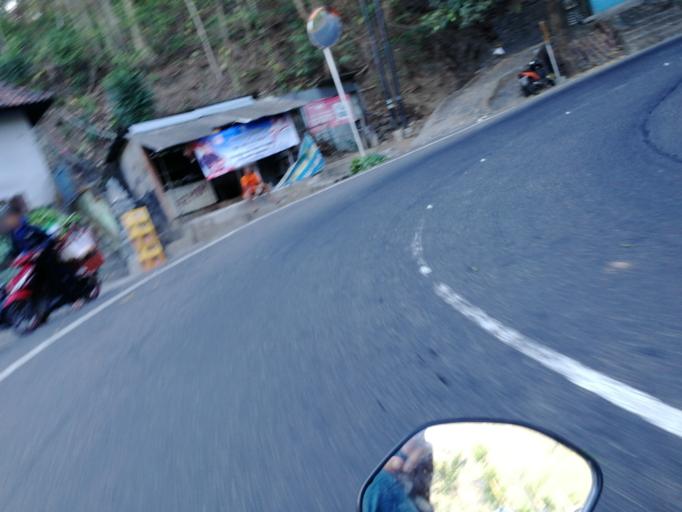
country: ID
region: Bali
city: Banjar Kangkaang
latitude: -8.3673
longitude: 115.6134
